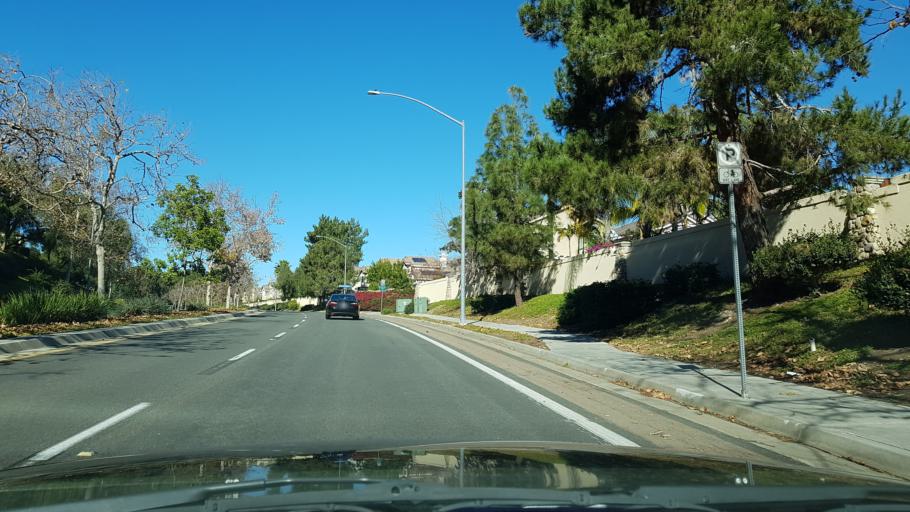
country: US
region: California
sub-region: San Diego County
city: Poway
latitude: 32.9754
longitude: -117.0691
